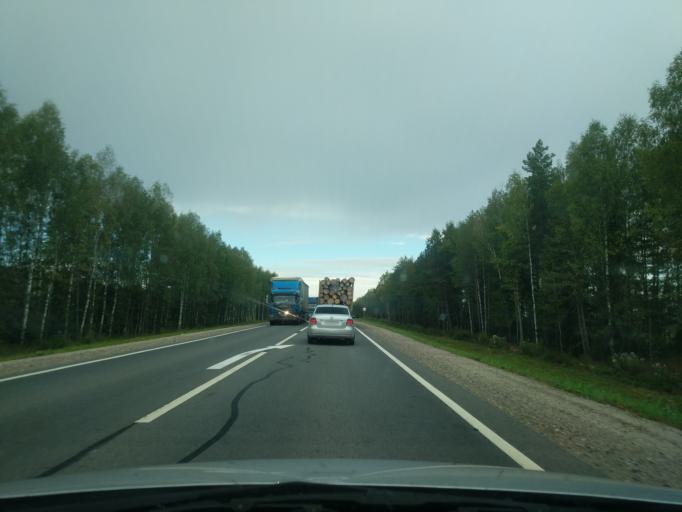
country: RU
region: Kostroma
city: Ostrovskoye
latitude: 57.8070
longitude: 42.3032
